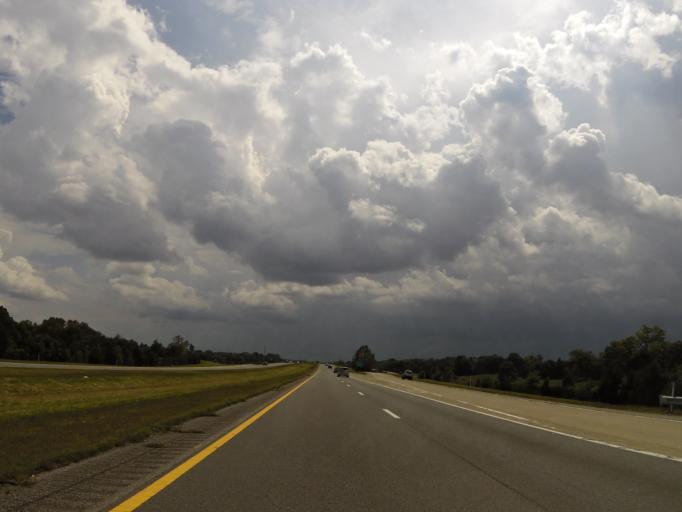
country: US
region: Tennessee
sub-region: Wilson County
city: Rural Hill
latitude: 36.1167
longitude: -86.4081
